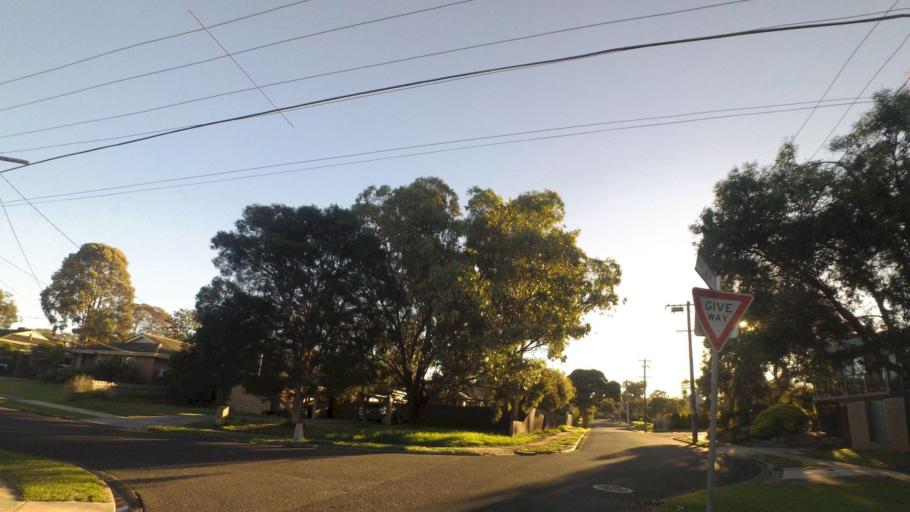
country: AU
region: Victoria
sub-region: Banyule
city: Yallambie
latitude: -37.7312
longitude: 145.0976
